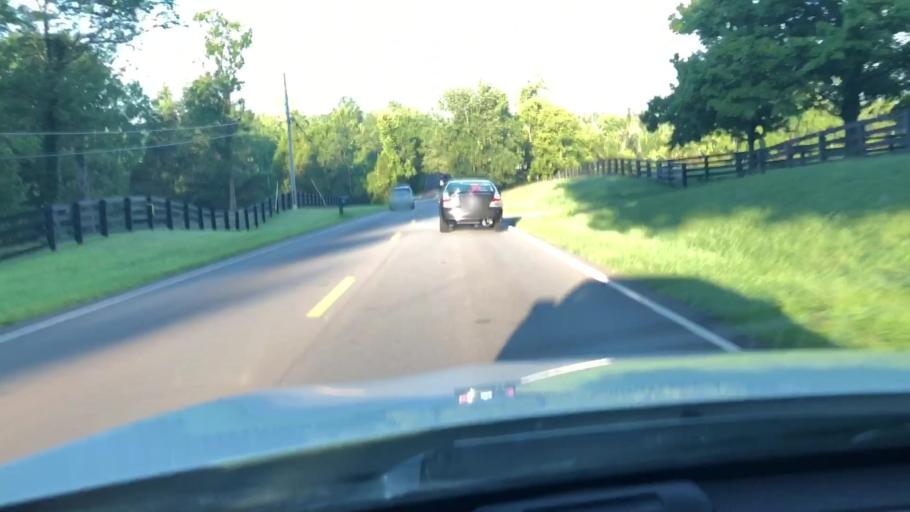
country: US
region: Kentucky
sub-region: Jefferson County
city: Middletown
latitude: 38.2198
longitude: -85.5169
